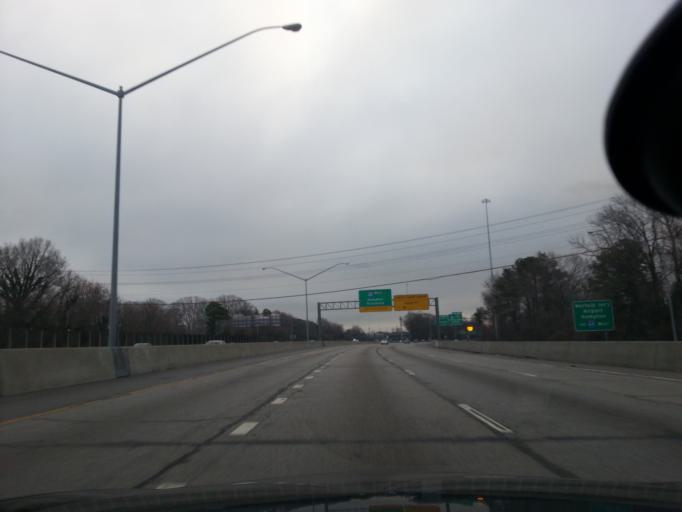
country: US
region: Virginia
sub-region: City of Chesapeake
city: Chesapeake
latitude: 36.8441
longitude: -76.2076
